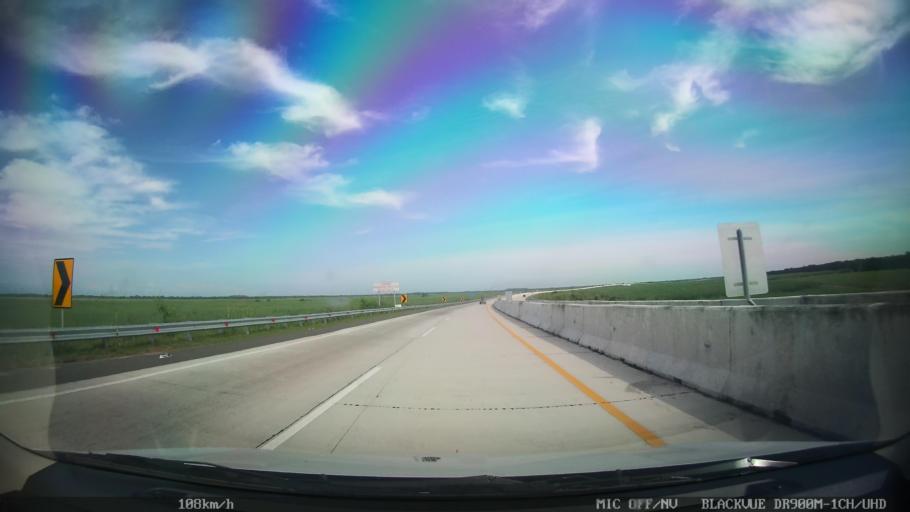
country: ID
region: North Sumatra
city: Binjai
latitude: 3.6549
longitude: 98.5350
